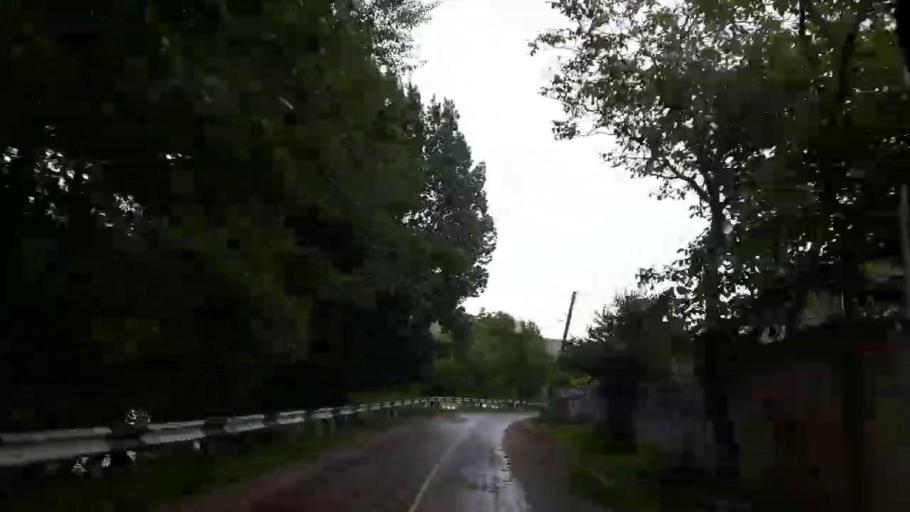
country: GE
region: Shida Kartli
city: Gori
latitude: 41.9663
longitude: 44.2171
